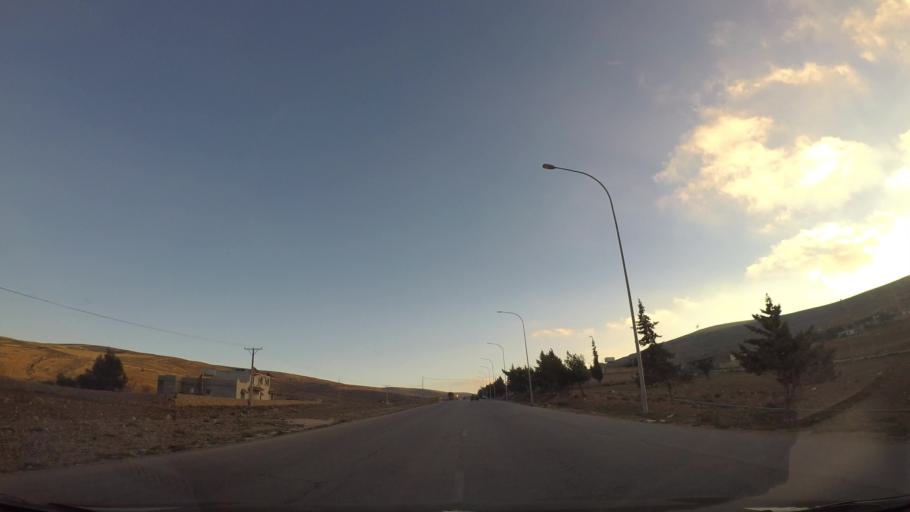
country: JO
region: Ma'an
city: Petra
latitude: 30.4333
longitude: 35.5164
